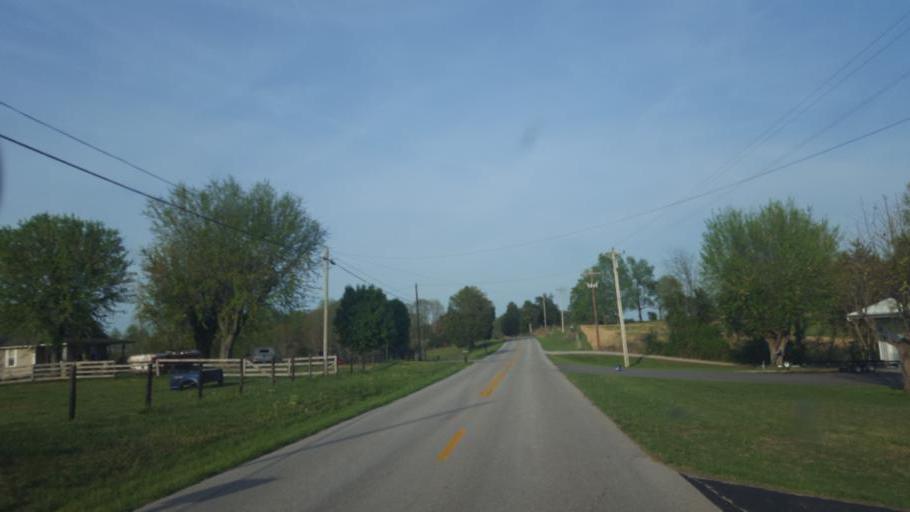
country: US
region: Kentucky
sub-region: Allen County
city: Scottsville
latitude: 36.9174
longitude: -86.1009
